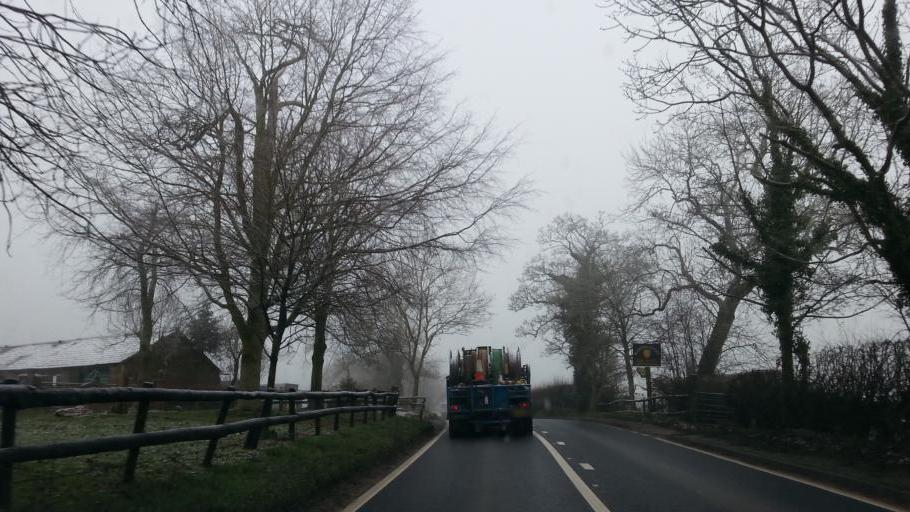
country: GB
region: England
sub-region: Cheshire East
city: Siddington
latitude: 53.2140
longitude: -2.2293
